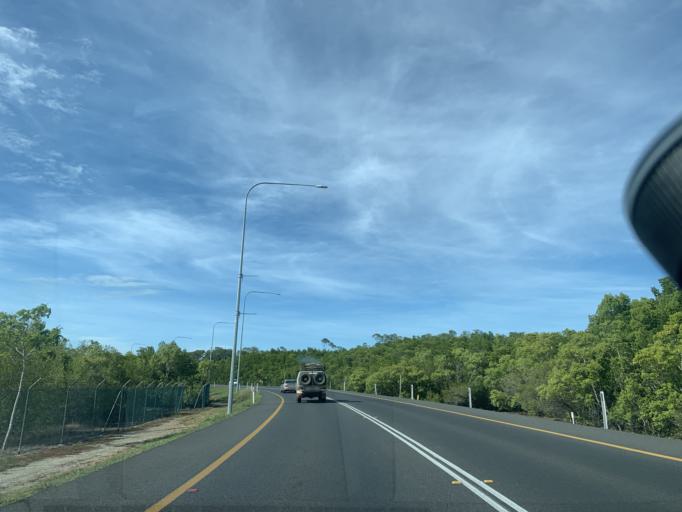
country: AU
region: Queensland
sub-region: Cairns
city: Cairns
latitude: -16.8880
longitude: 145.7622
